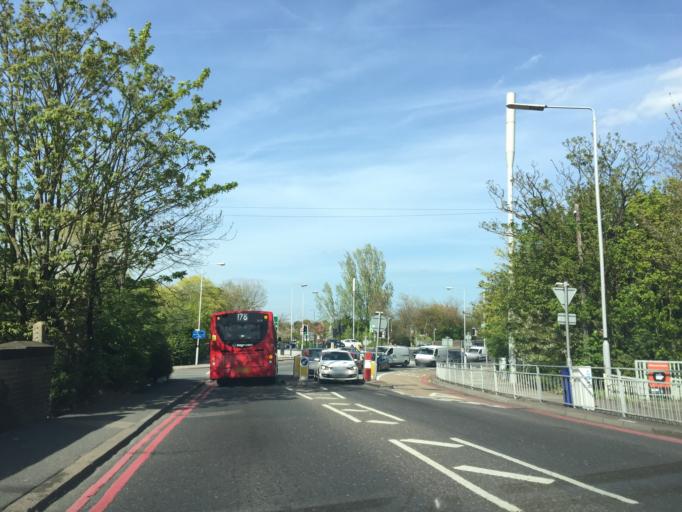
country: GB
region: England
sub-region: Greater London
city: Blackheath
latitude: 51.4625
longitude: 0.0265
